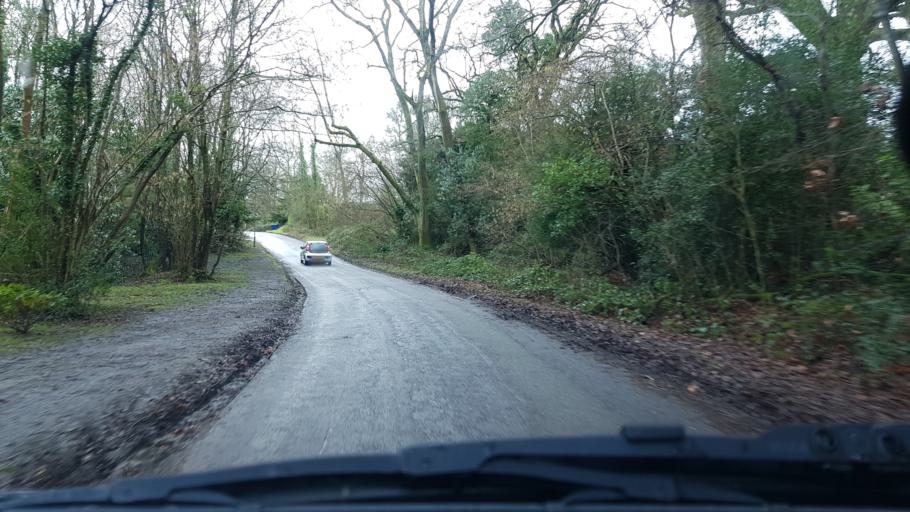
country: GB
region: England
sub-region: Surrey
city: Haslemere
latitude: 51.0999
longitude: -0.6881
